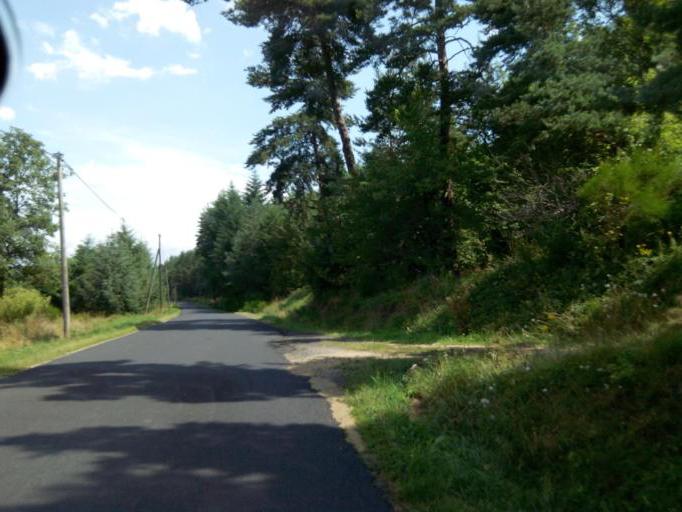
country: FR
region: Rhone-Alpes
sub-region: Departement de la Loire
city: Usson-en-Forez
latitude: 45.3635
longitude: 3.9595
